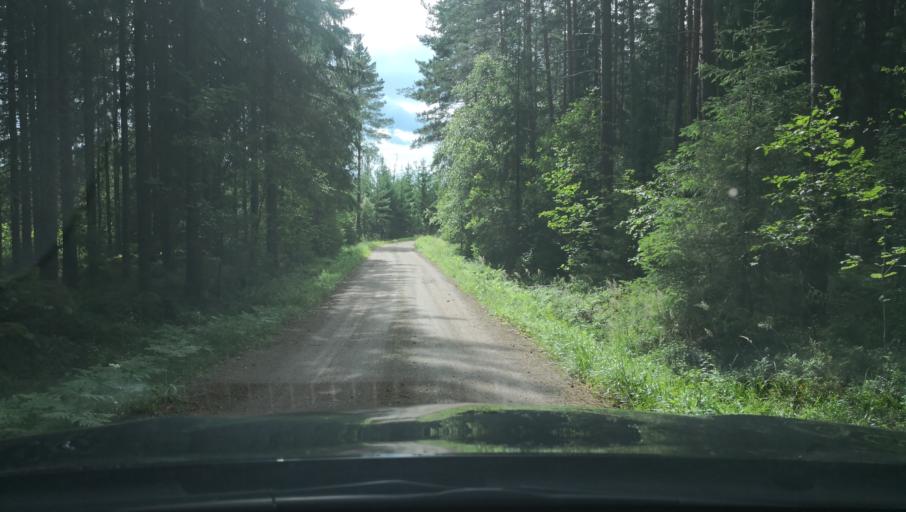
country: SE
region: Vaestmanland
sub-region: Hallstahammars Kommun
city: Hallstahammar
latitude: 59.6488
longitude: 16.0929
